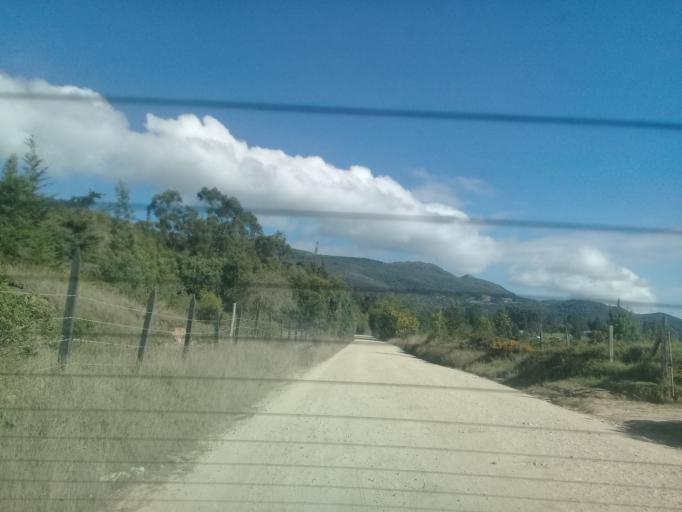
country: CO
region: Cundinamarca
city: Tocancipa
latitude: 4.9197
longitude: -73.8853
